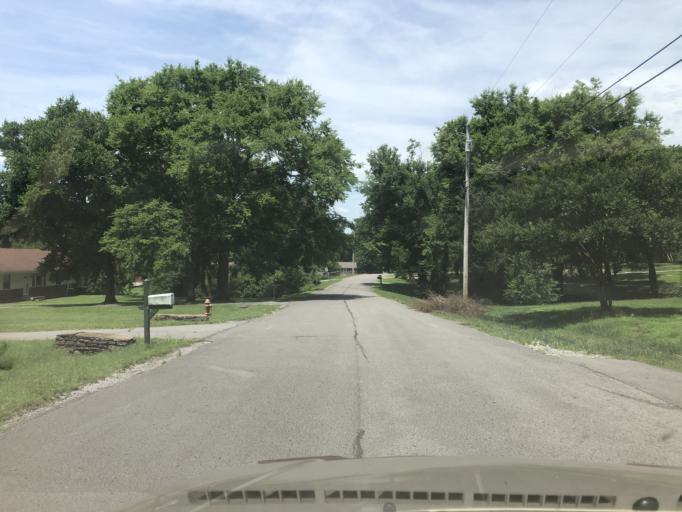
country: US
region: Tennessee
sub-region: Davidson County
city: Lakewood
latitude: 36.2481
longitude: -86.6878
